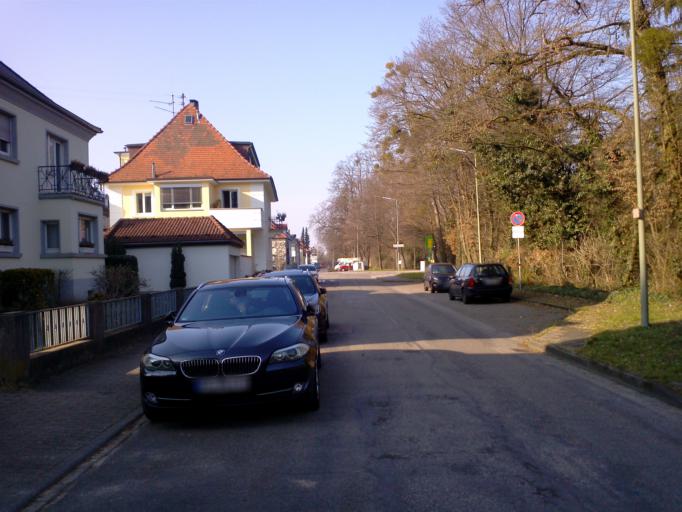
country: DE
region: Baden-Wuerttemberg
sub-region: Karlsruhe Region
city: Karlsruhe
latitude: 48.9833
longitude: 8.3964
